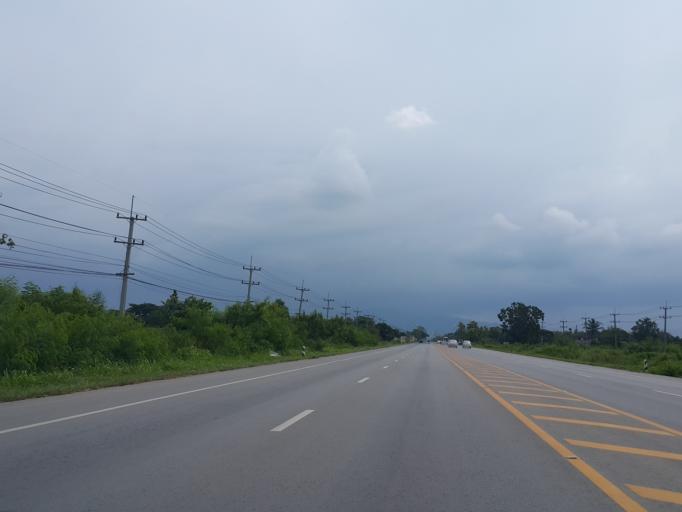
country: TH
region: Chiang Mai
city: San Kamphaeng
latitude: 18.7297
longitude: 99.0976
